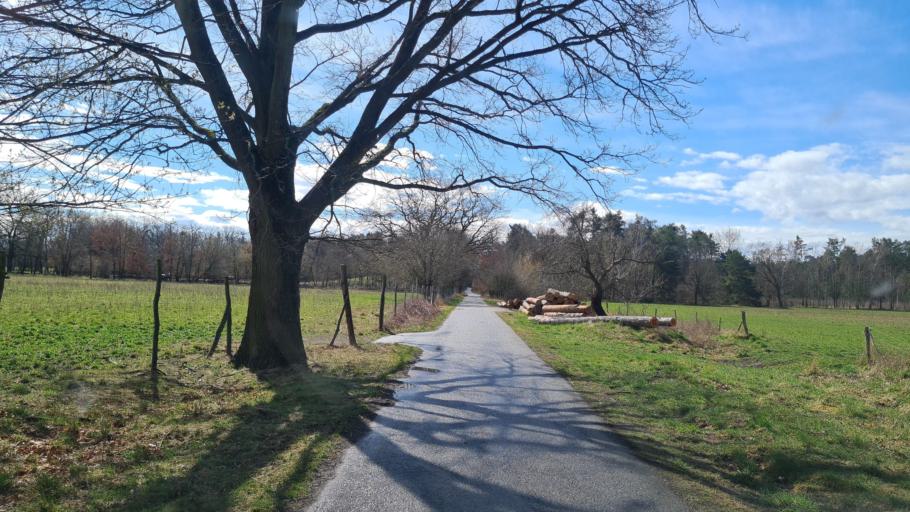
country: DE
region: Brandenburg
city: Altdobern
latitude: 51.7085
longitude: 14.0376
